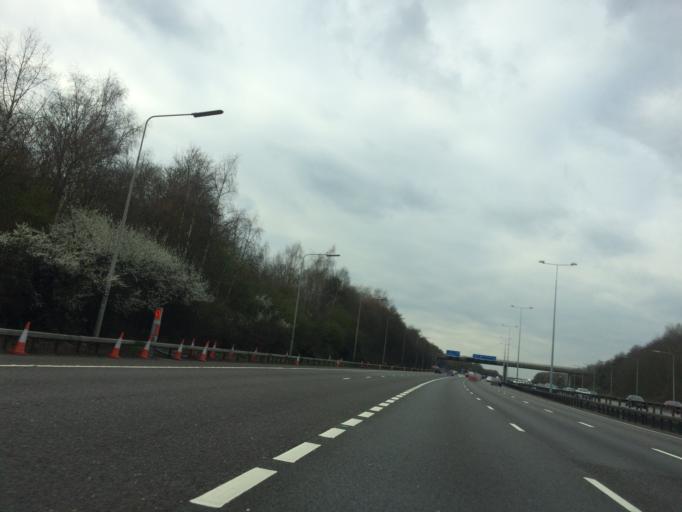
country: GB
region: England
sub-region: Surrey
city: Chertsey
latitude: 51.3935
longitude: -0.5331
